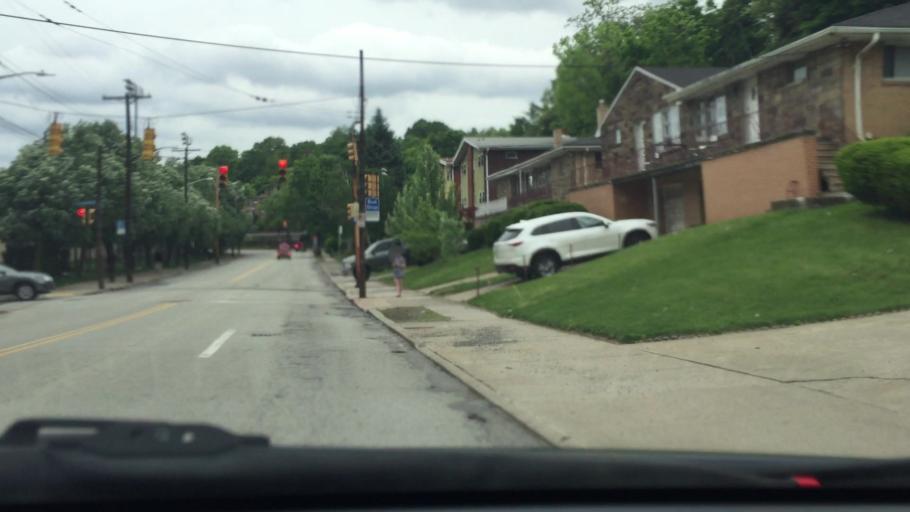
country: US
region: Pennsylvania
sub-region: Allegheny County
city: Bloomfield
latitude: 40.4425
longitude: -79.9373
